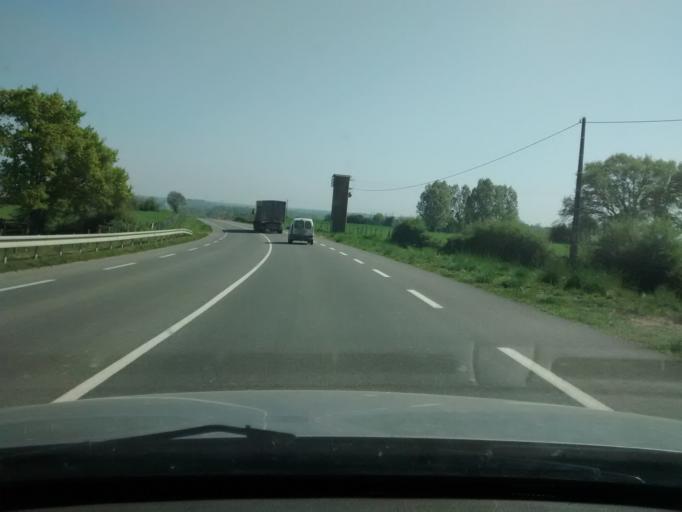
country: FR
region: Pays de la Loire
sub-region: Departement de la Mayenne
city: Soulge-sur-Ouette
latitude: 48.0714
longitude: -0.5564
